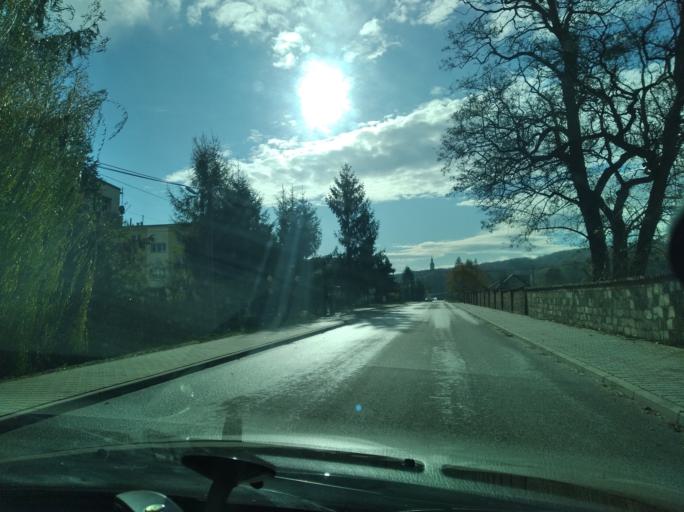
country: PL
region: Subcarpathian Voivodeship
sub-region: Powiat debicki
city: Brzeznica
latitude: 50.0559
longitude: 21.4842
